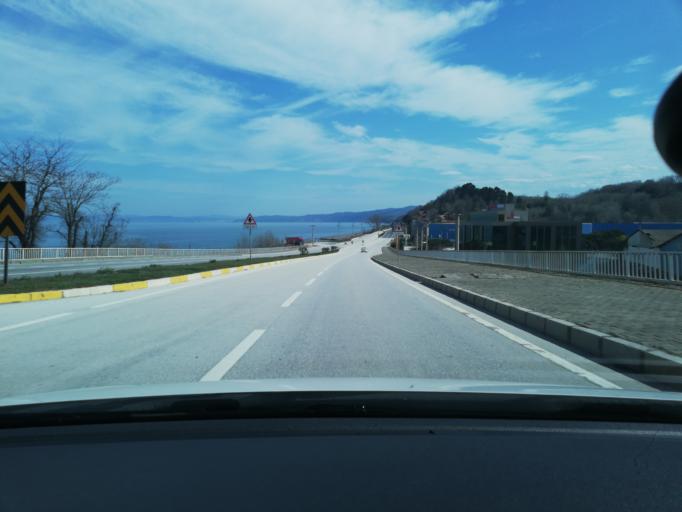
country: TR
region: Duzce
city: Akcakoca
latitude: 41.0944
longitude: 31.1938
